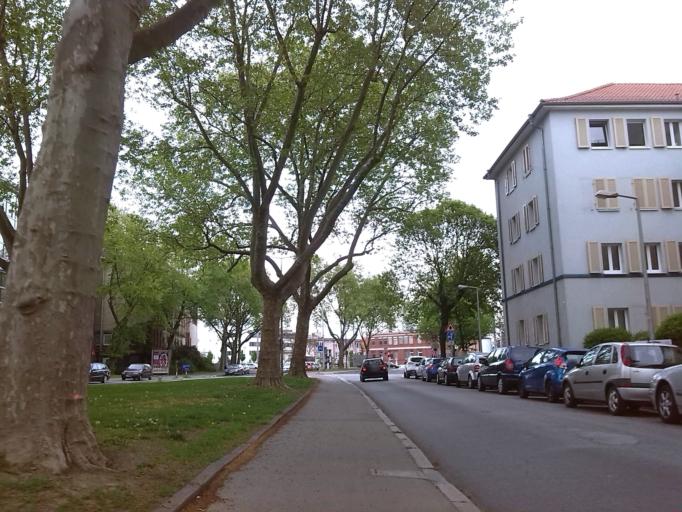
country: DE
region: Baden-Wuerttemberg
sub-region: Karlsruhe Region
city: Mannheim
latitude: 49.4678
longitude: 8.4823
